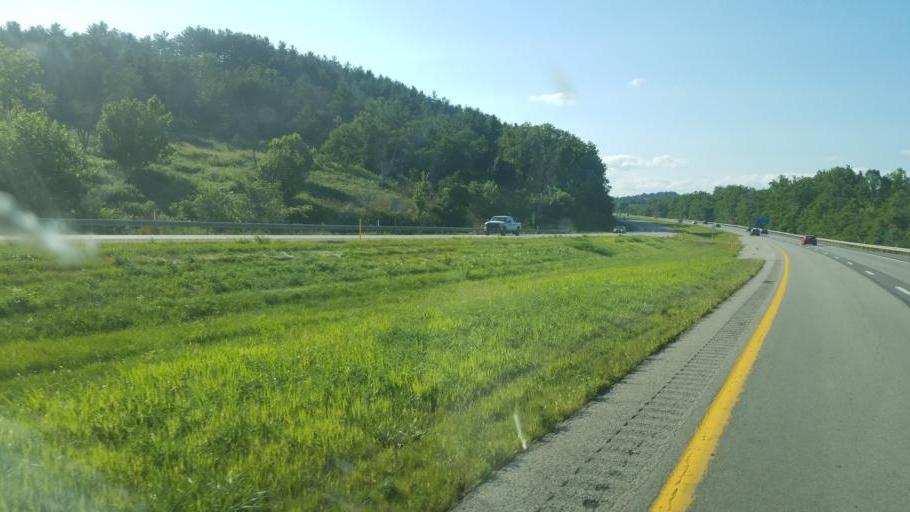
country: US
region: Pennsylvania
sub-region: Washington County
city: East Washington
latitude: 40.0996
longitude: -80.1943
